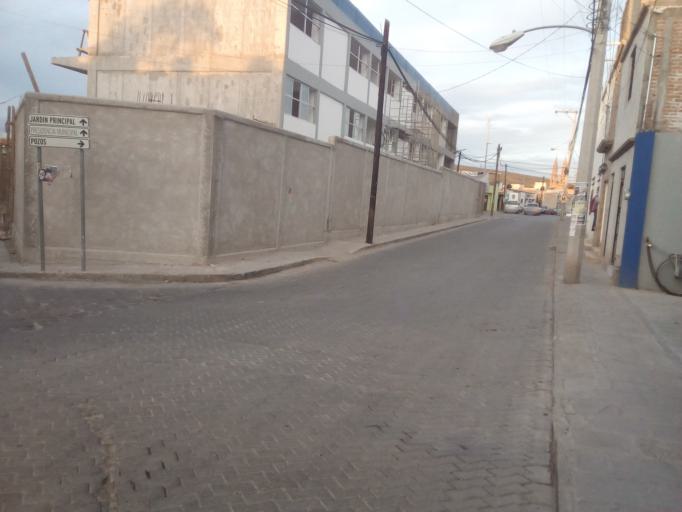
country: MX
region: Guerrero
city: San Luis de la Paz
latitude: 21.2951
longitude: -100.5151
